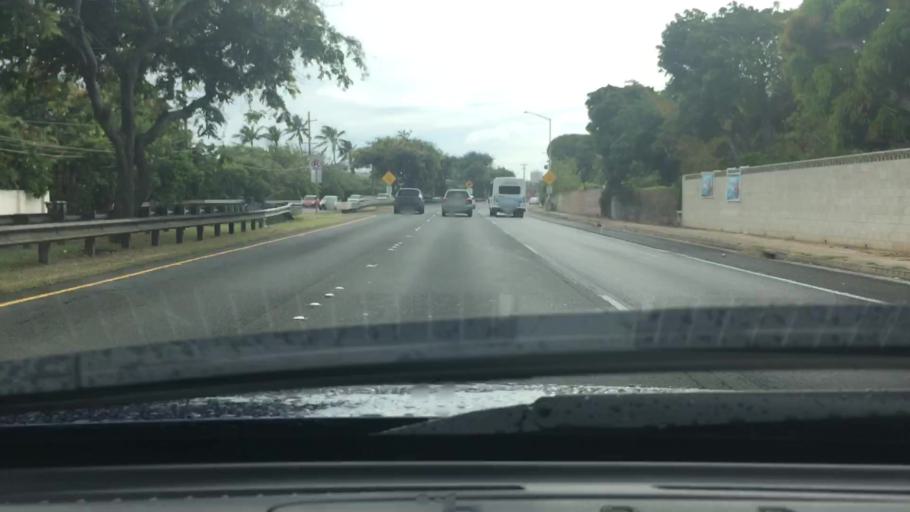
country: US
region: Hawaii
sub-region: Honolulu County
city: Waimanalo
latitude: 21.2762
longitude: -157.7647
